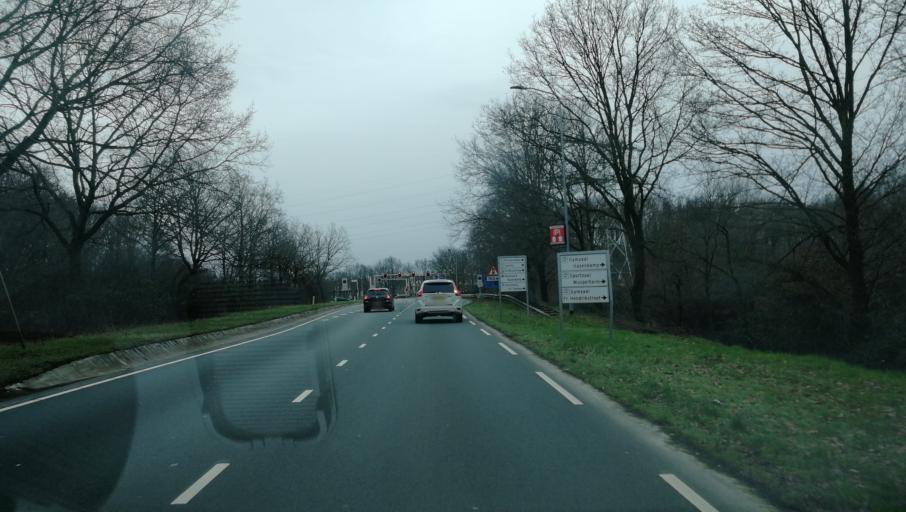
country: NL
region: Limburg
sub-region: Gemeente Venlo
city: Venlo
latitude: 51.3808
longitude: 6.1349
